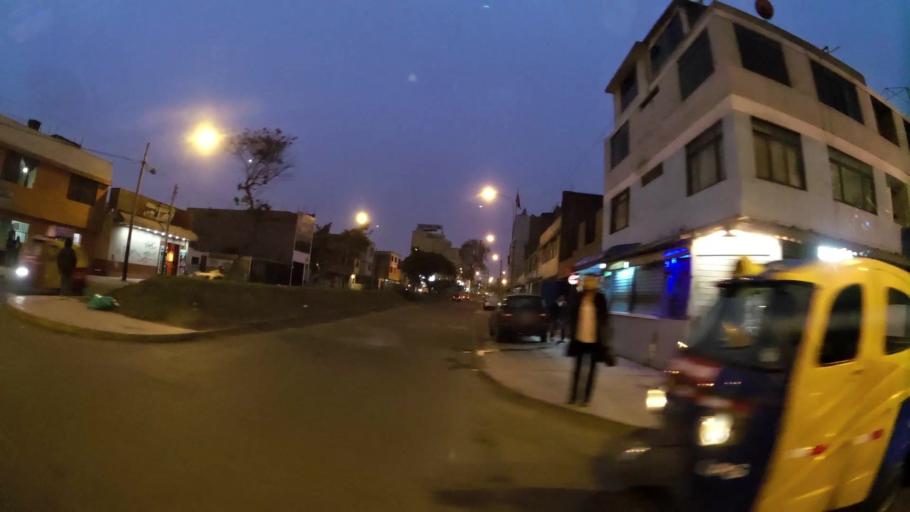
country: PE
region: Lima
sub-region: Lima
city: Surco
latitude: -12.1671
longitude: -76.9690
